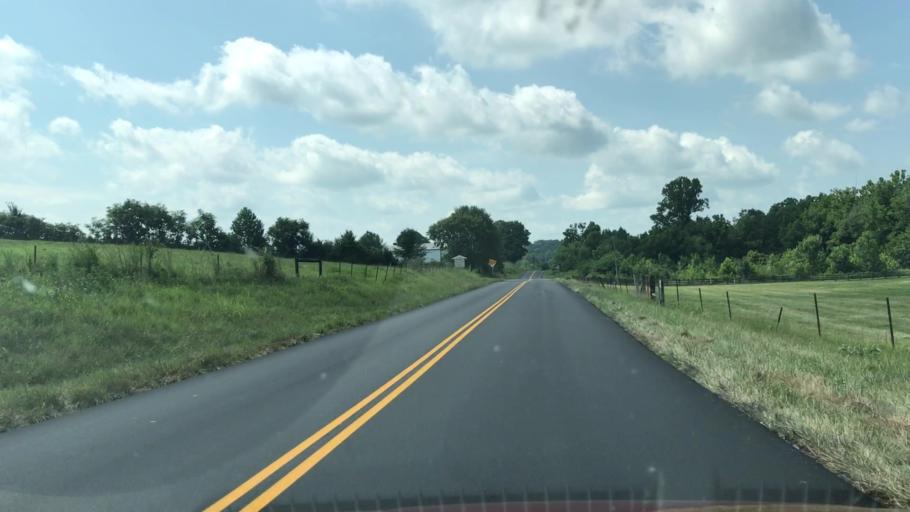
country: US
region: Kentucky
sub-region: Monroe County
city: Tompkinsville
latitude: 36.7740
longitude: -85.7990
